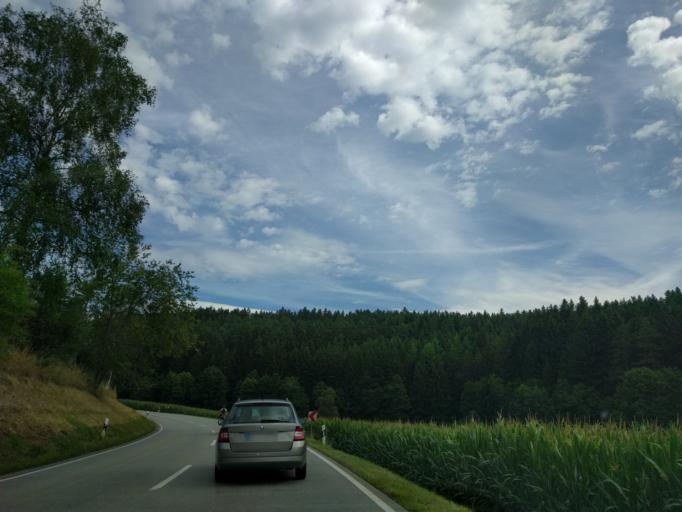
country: DE
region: Bavaria
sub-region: Lower Bavaria
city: Bischofsmais
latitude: 48.9386
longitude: 13.1074
